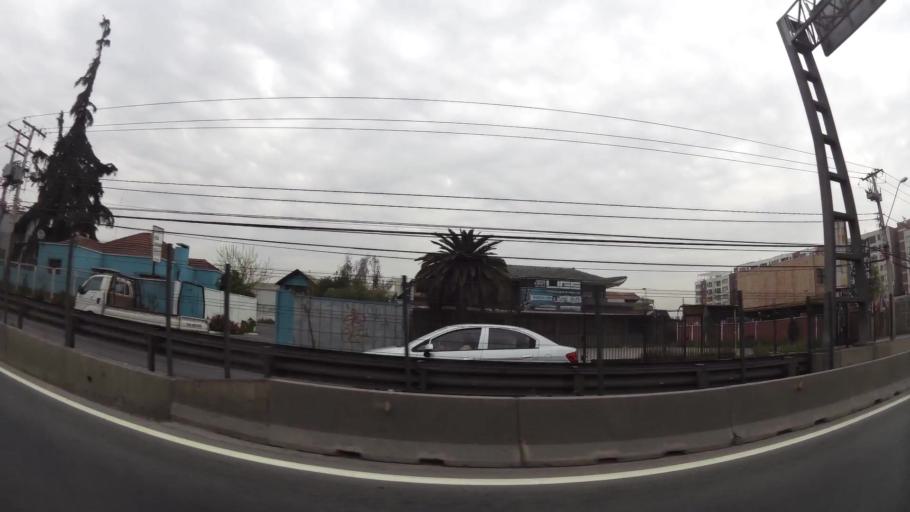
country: CL
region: Santiago Metropolitan
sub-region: Provincia de Santiago
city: La Pintana
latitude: -33.5364
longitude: -70.6678
